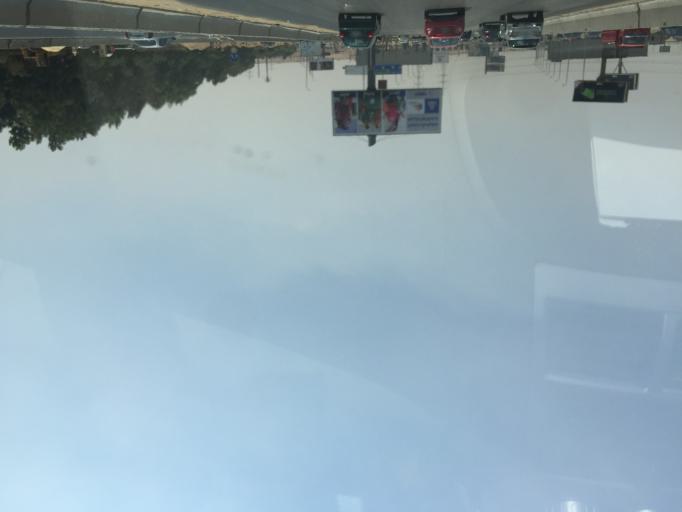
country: EG
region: Muhafazat al Qalyubiyah
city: Al Khankah
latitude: 30.0737
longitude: 31.4317
